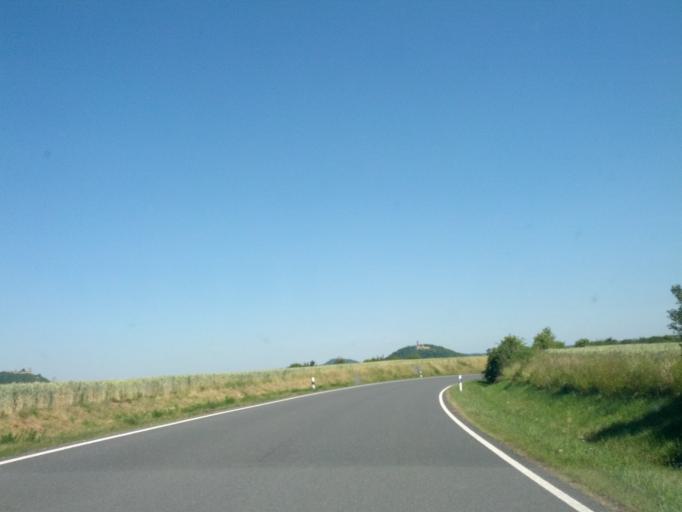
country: DE
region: Thuringia
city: Seebergen
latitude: 50.8808
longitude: 10.8033
